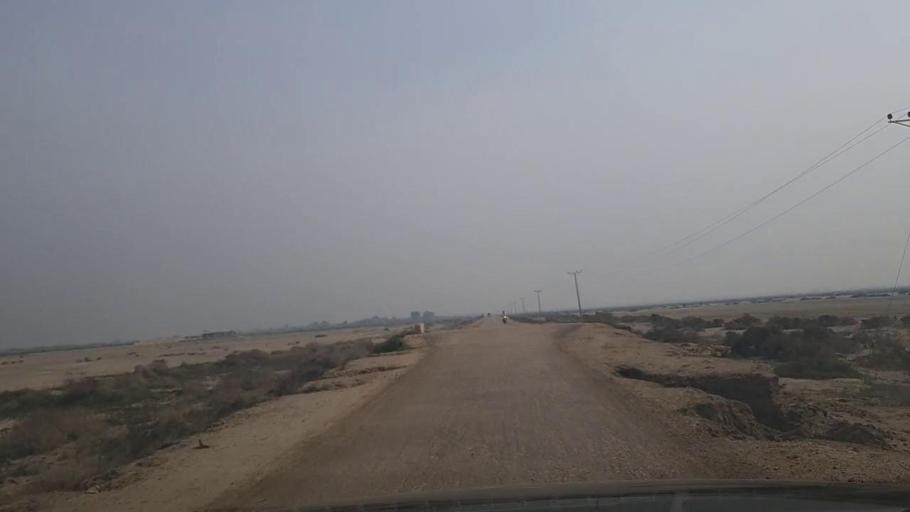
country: PK
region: Sindh
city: Mirpur Sakro
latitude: 24.4643
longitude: 67.6873
